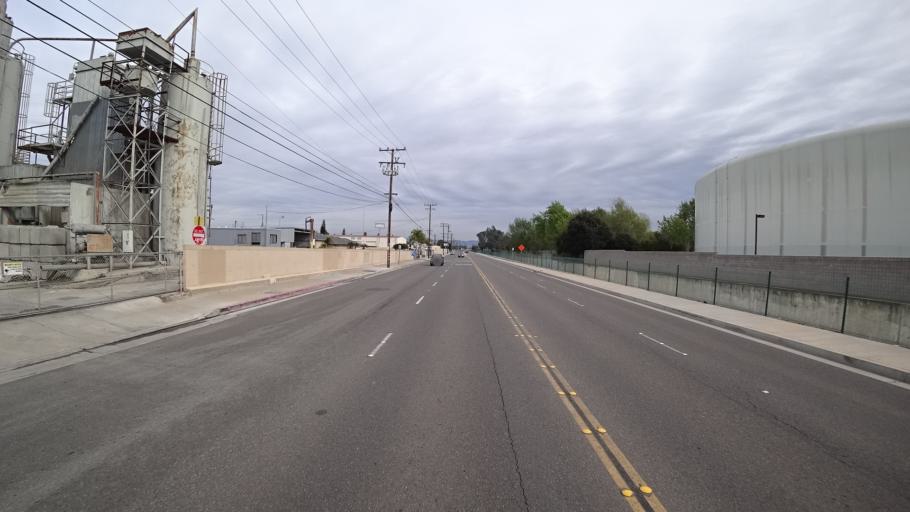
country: US
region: California
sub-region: Orange County
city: Midway City
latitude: 33.7520
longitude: -117.9973
